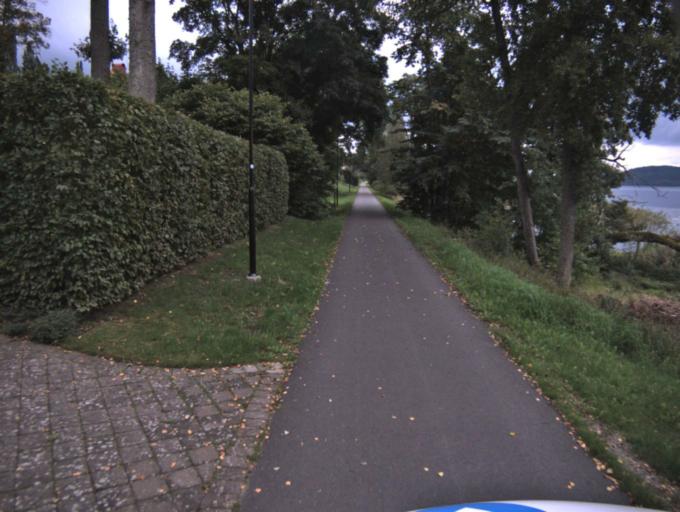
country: SE
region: Vaestra Goetaland
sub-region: Ulricehamns Kommun
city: Ulricehamn
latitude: 57.7817
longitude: 13.4039
